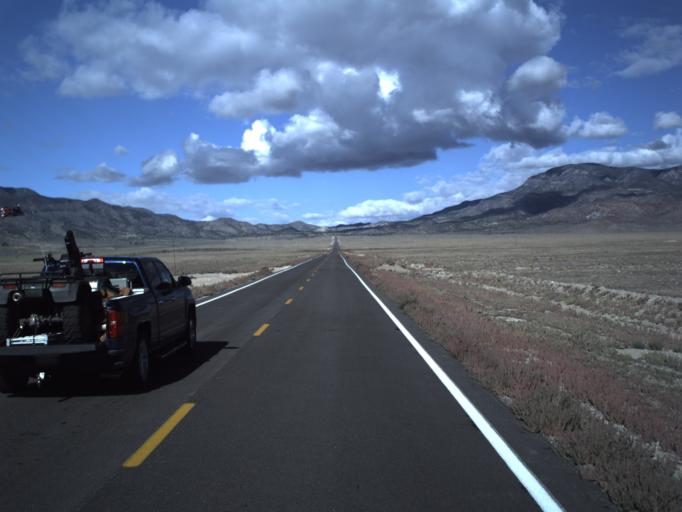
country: US
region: Utah
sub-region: Beaver County
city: Milford
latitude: 38.4809
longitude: -113.4389
